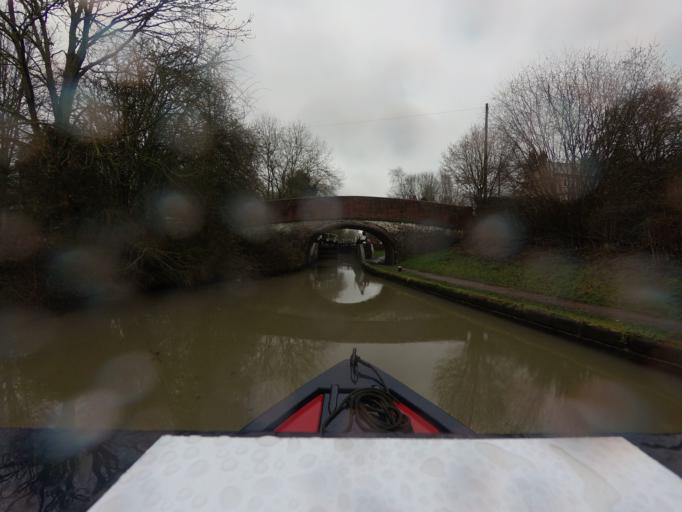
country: GB
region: England
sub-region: Northamptonshire
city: Daventry
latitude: 52.2864
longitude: -1.1918
